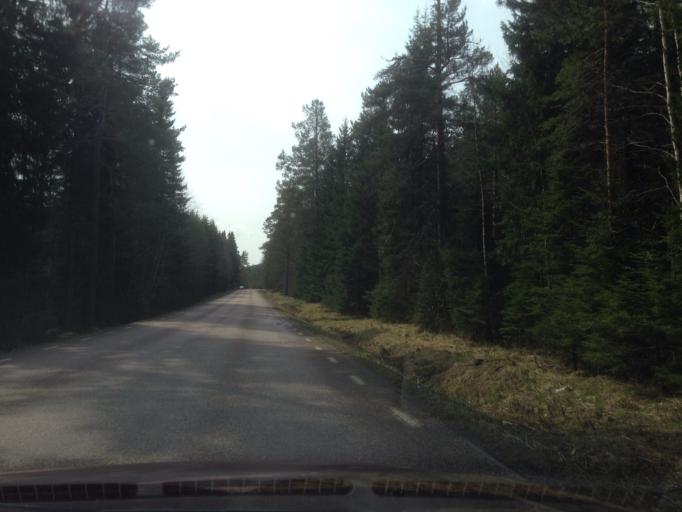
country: SE
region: Dalarna
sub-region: Ludvika Kommun
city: Grangesberg
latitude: 60.1130
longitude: 15.0100
